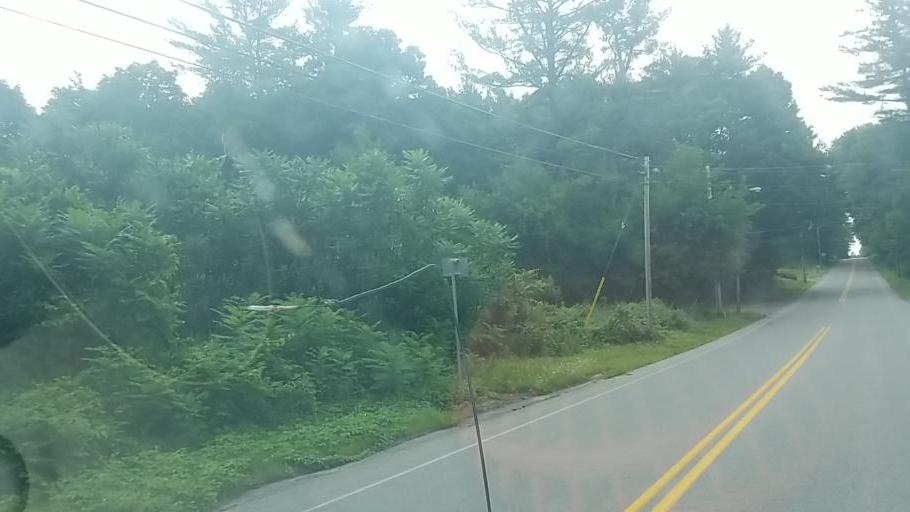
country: US
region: New York
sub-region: Fulton County
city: Gloversville
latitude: 43.0426
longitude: -74.3789
